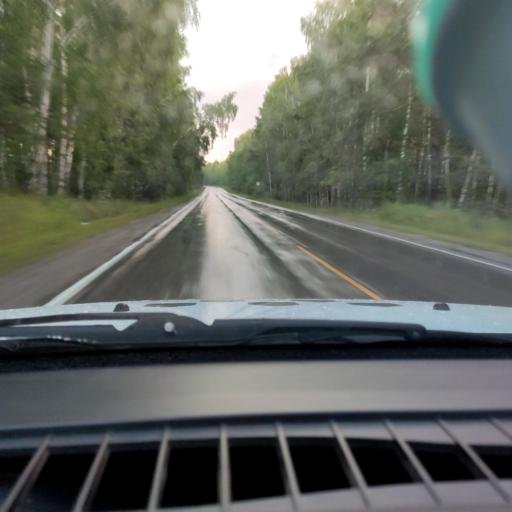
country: RU
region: Chelyabinsk
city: Ozersk
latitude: 55.8077
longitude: 60.6285
